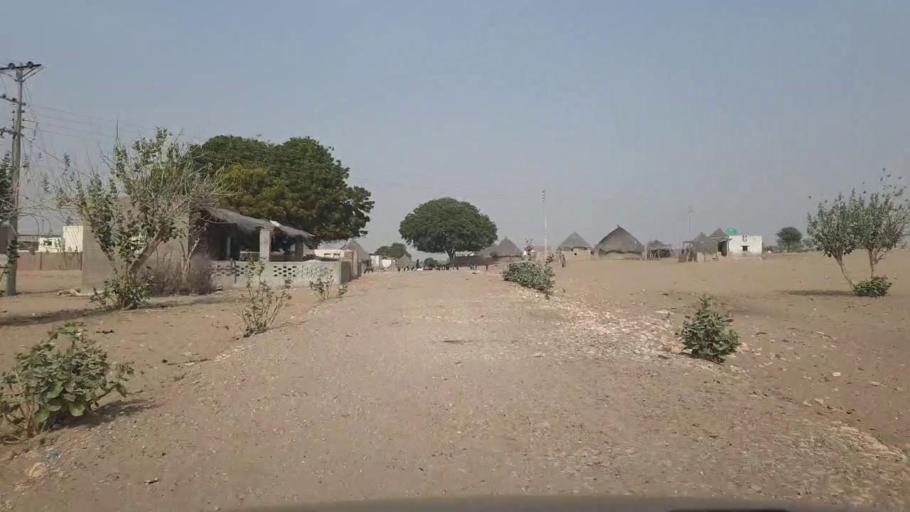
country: PK
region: Sindh
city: Chor
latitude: 25.6410
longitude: 70.0545
